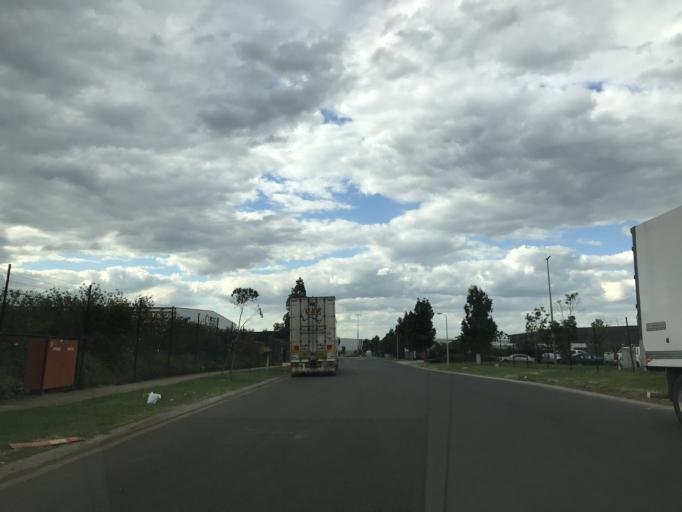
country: AU
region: Victoria
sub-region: Wyndham
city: Truganina
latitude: -37.8229
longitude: 144.7445
